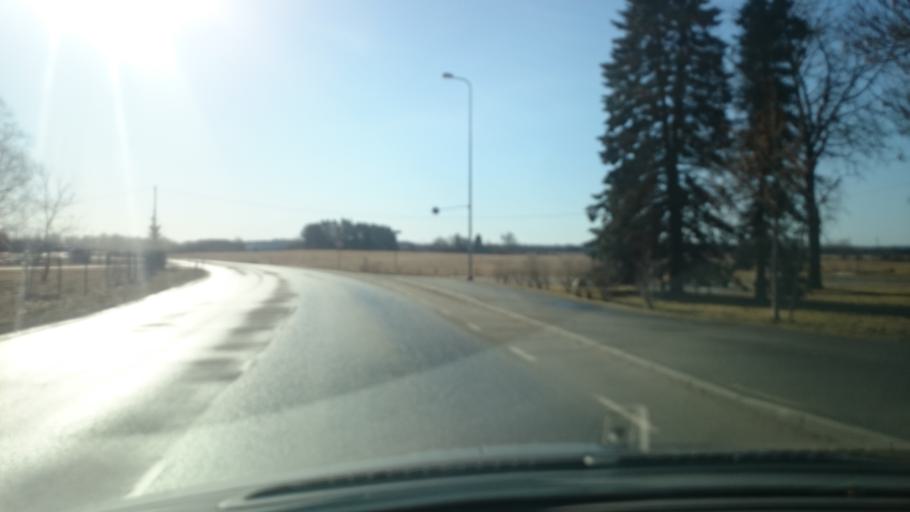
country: EE
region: Harju
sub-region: Saku vald
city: Saku
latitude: 59.2737
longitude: 24.7207
